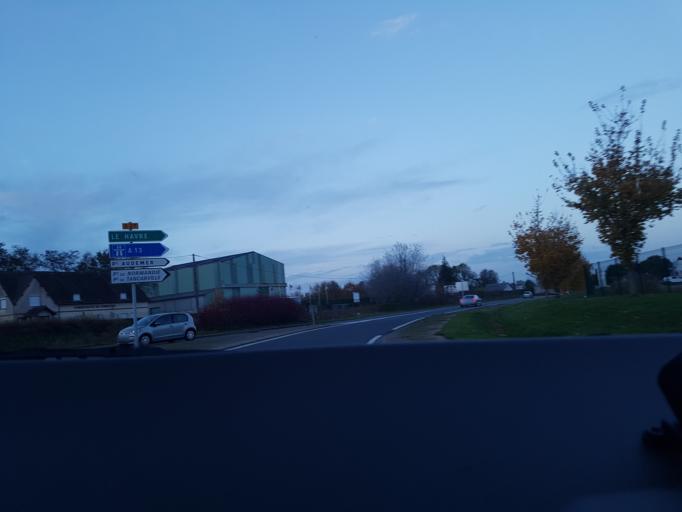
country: FR
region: Haute-Normandie
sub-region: Departement de l'Eure
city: Beuzeville
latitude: 49.3407
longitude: 0.3579
